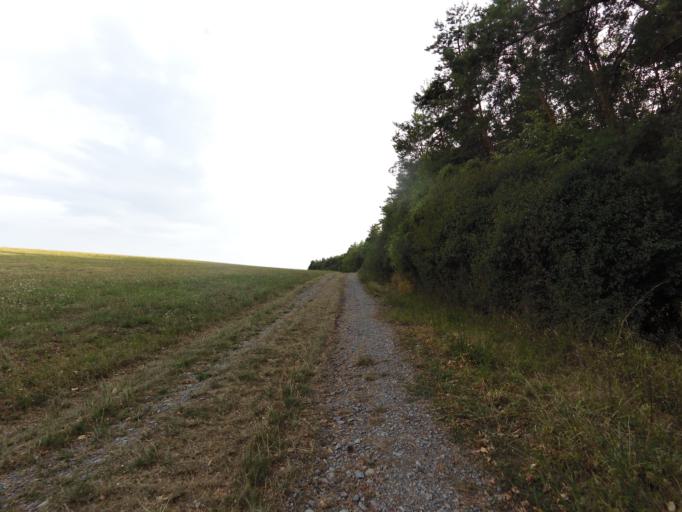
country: DE
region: Bavaria
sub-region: Regierungsbezirk Unterfranken
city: Zell am Main
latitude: 49.8048
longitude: 9.8692
